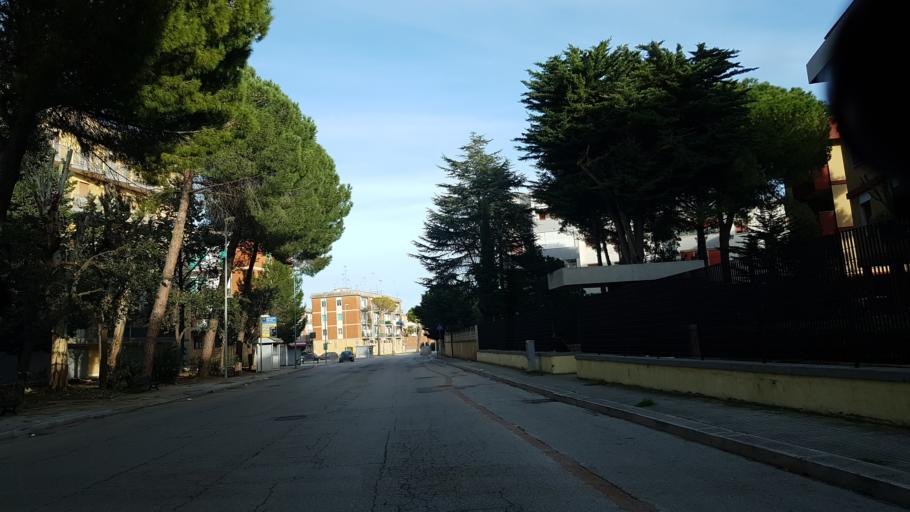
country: IT
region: Apulia
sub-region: Provincia di Brindisi
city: Brindisi
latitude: 40.6191
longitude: 17.9231
